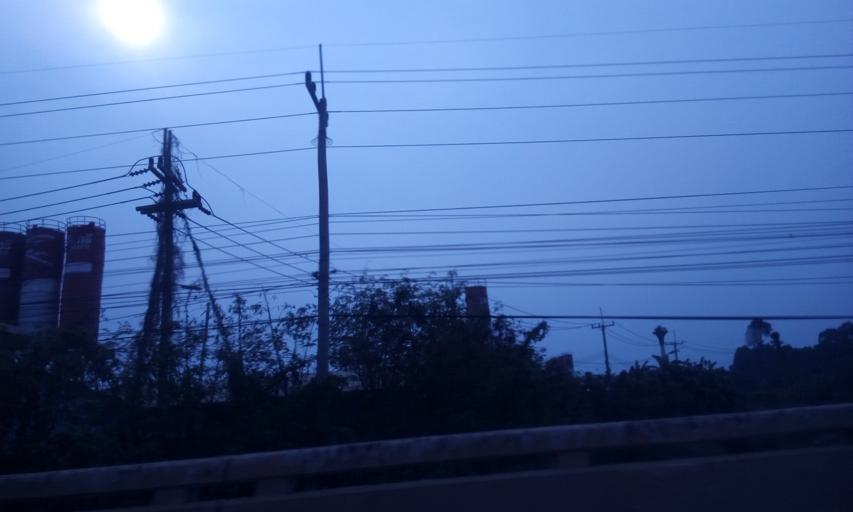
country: TH
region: Chachoengsao
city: Plaeng Yao
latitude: 13.5659
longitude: 101.2681
